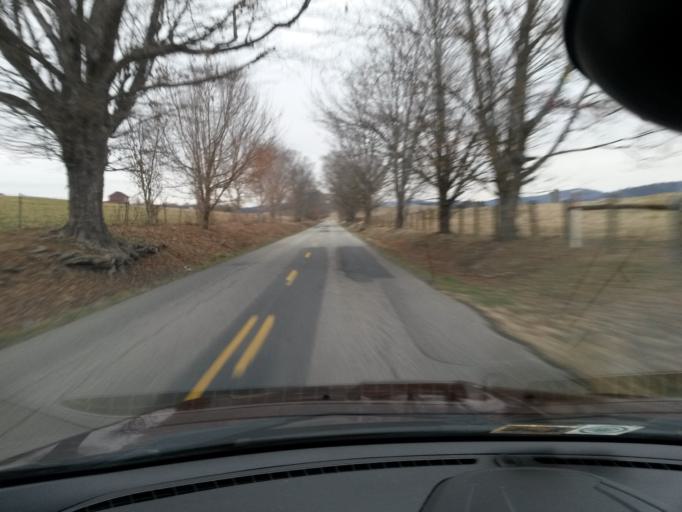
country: US
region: Virginia
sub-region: Rockbridge County
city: East Lexington
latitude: 37.9134
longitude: -79.3213
